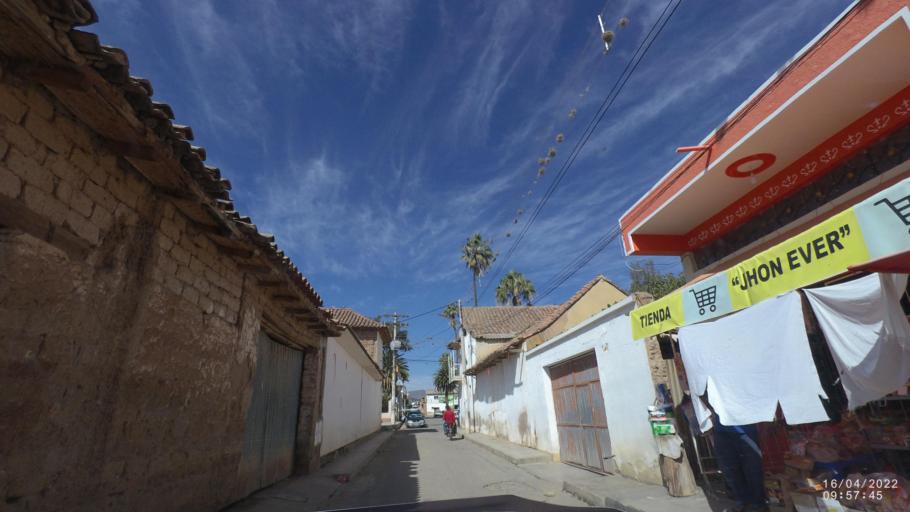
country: BO
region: Cochabamba
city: Cliza
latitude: -17.6263
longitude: -65.9265
